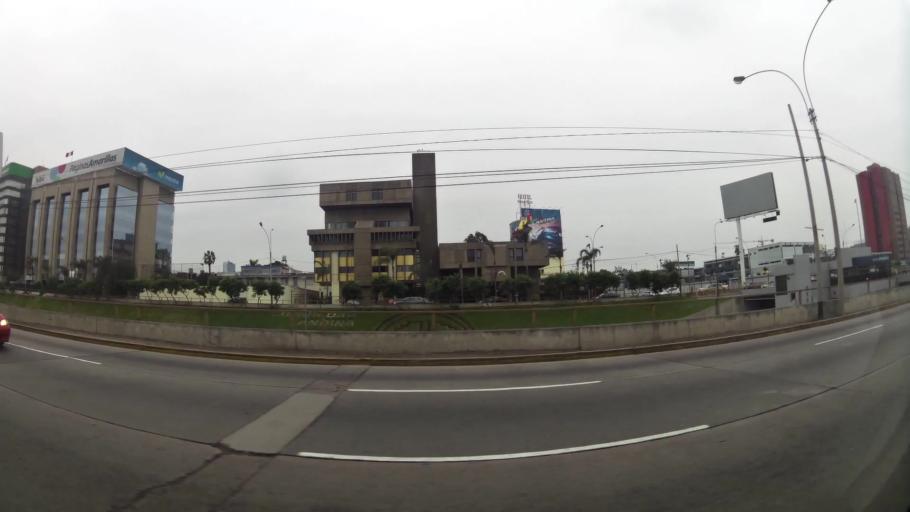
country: PE
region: Lima
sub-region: Lima
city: San Isidro
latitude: -12.1022
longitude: -77.0276
